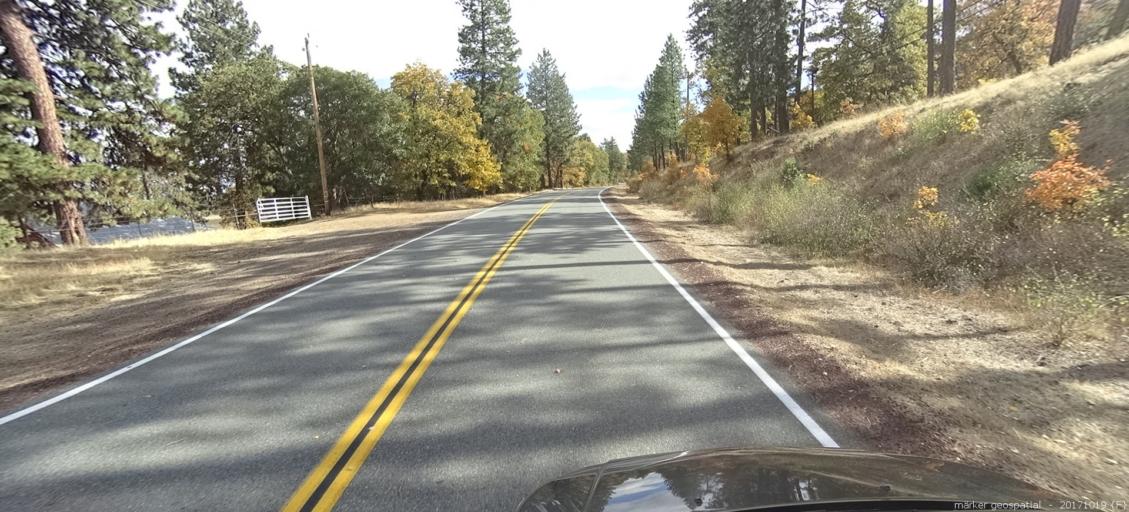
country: US
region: California
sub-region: Shasta County
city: Burney
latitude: 41.0325
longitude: -121.4854
